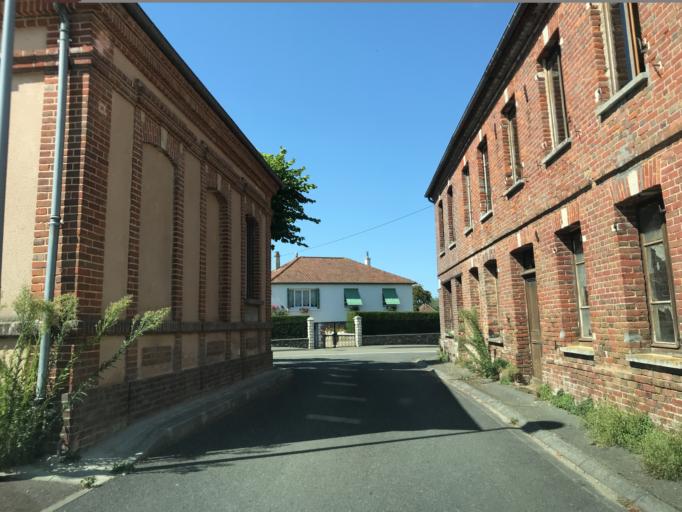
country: FR
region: Haute-Normandie
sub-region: Departement de l'Eure
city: Normanville
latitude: 49.0952
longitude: 1.2046
